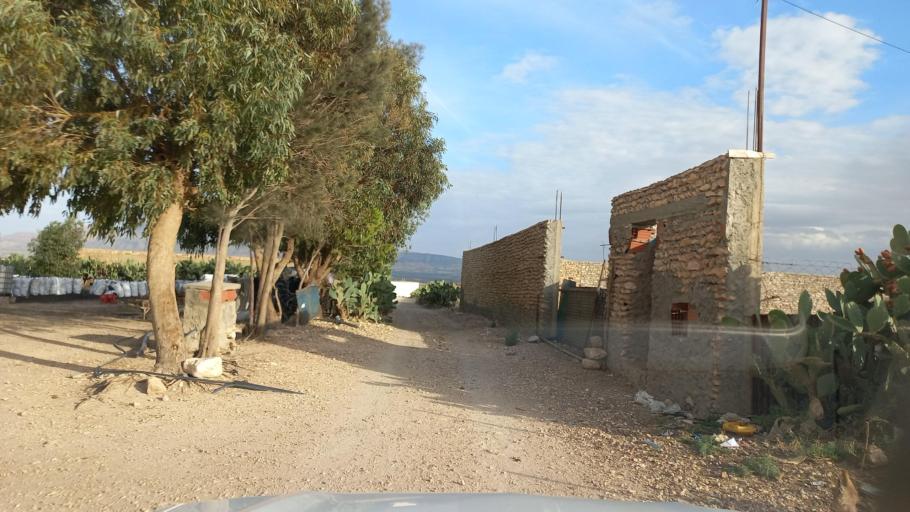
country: TN
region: Al Qasrayn
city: Sbiba
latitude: 35.4543
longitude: 9.0858
